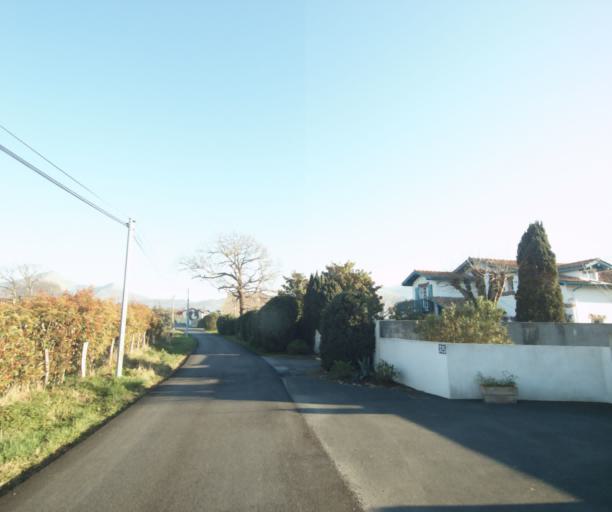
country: FR
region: Aquitaine
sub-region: Departement des Pyrenees-Atlantiques
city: Urrugne
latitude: 43.3455
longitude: -1.7021
